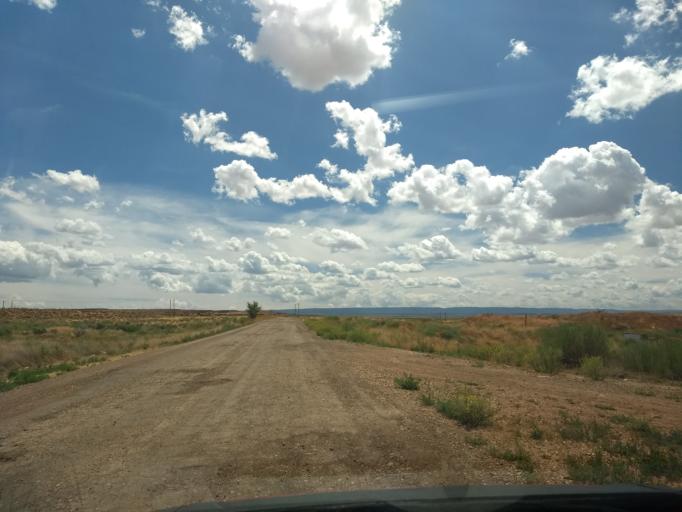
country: US
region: Arizona
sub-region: Coconino County
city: Fredonia
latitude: 36.9443
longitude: -112.5144
